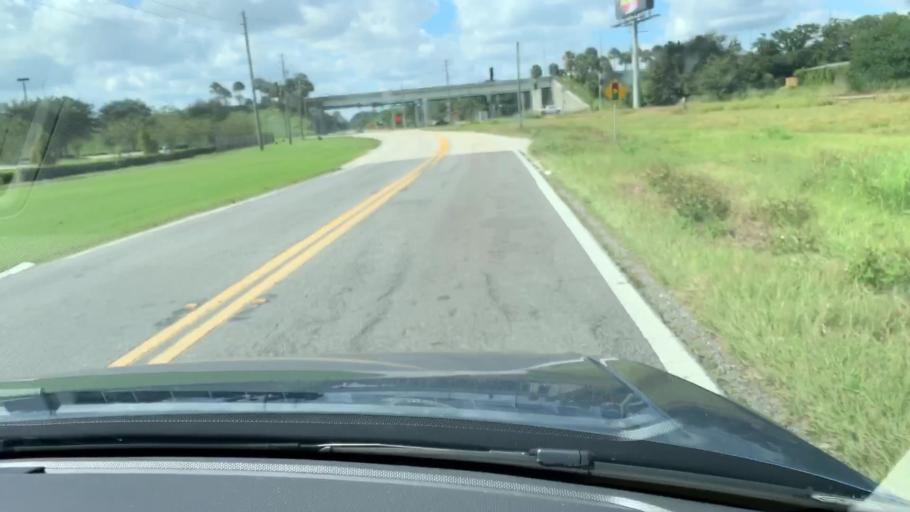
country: US
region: Florida
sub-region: Polk County
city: Winston
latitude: 28.0297
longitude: -82.0377
